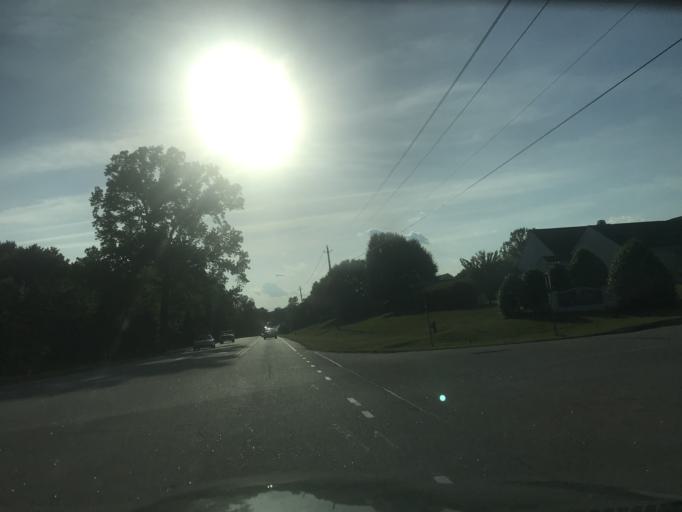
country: US
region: North Carolina
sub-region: Wake County
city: Knightdale
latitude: 35.7481
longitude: -78.4591
